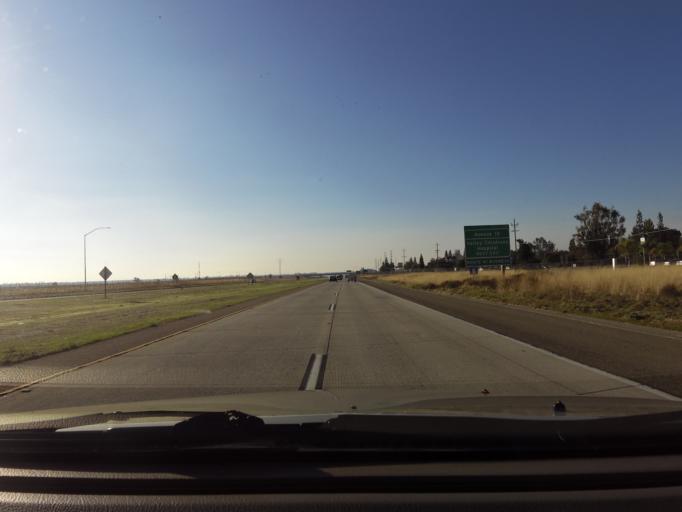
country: US
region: California
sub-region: Madera County
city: Bonadelle Ranchos-Madera Ranchos
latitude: 36.9025
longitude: -119.7928
